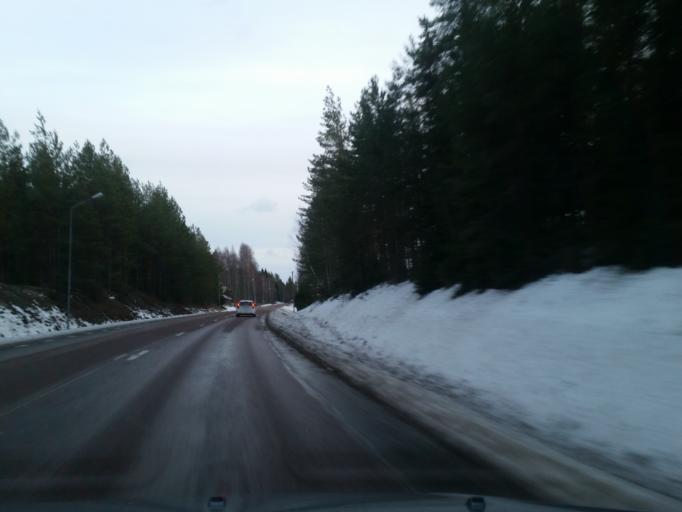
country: SE
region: Gaevleborg
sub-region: Sandvikens Kommun
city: Jarbo
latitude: 60.6951
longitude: 16.6326
